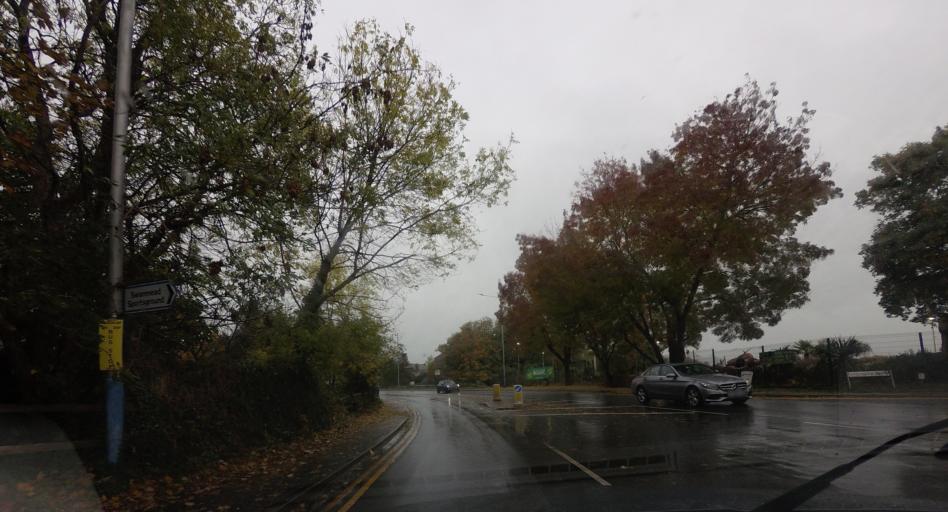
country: GB
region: England
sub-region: Kent
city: Tonbridge
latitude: 51.1985
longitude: 0.2837
